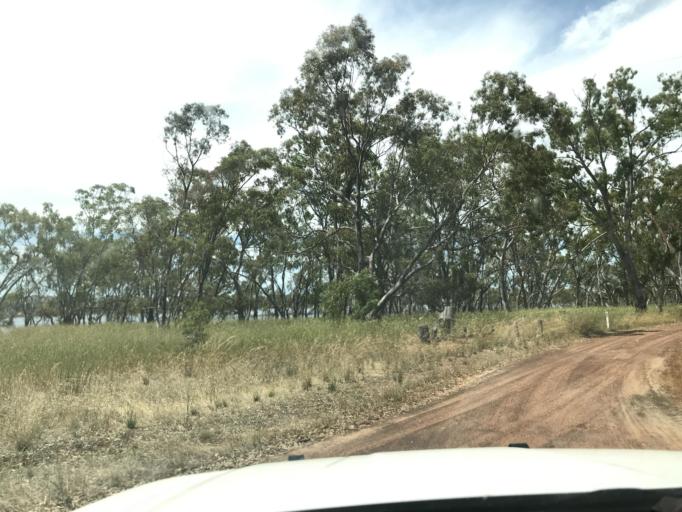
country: AU
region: Victoria
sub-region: Horsham
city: Horsham
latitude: -36.9925
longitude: 141.4967
